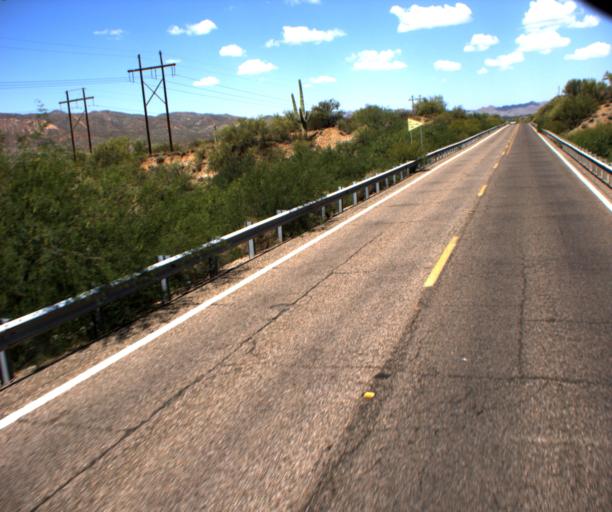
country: US
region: Arizona
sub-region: Pinal County
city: Kearny
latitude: 33.0147
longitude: -110.8329
